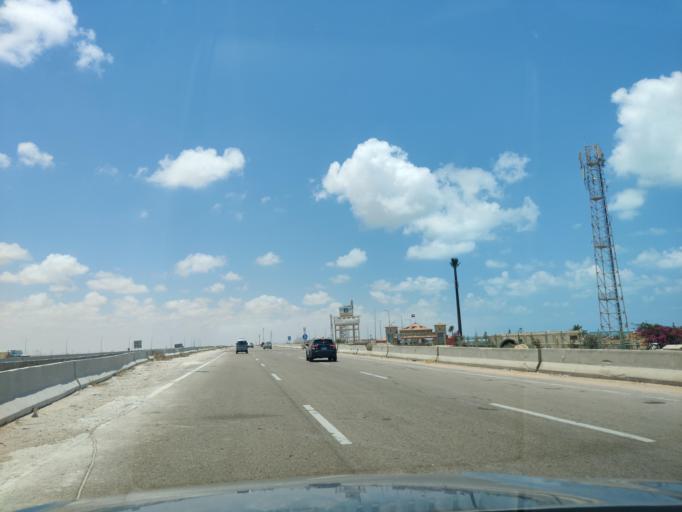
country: EG
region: Muhafazat Matruh
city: Al `Alamayn
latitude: 30.8128
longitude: 29.0587
